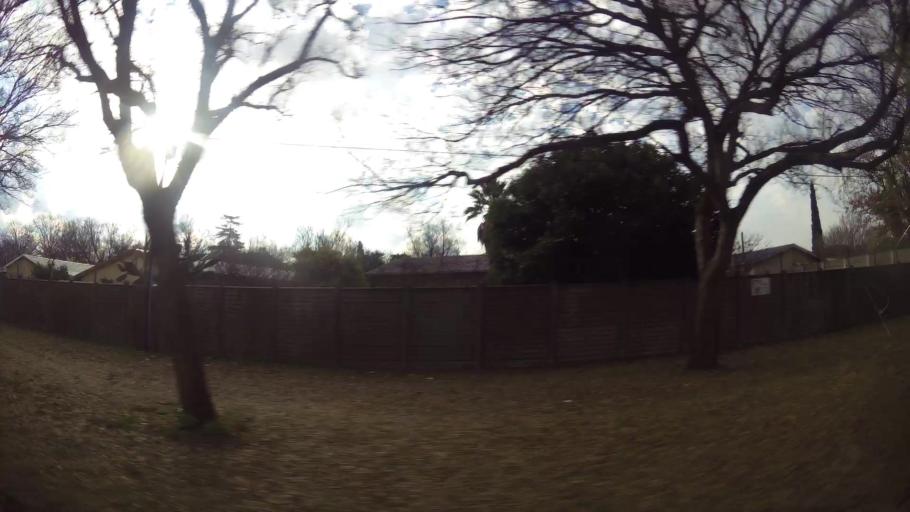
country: ZA
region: Orange Free State
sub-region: Fezile Dabi District Municipality
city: Sasolburg
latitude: -26.8177
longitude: 27.8186
